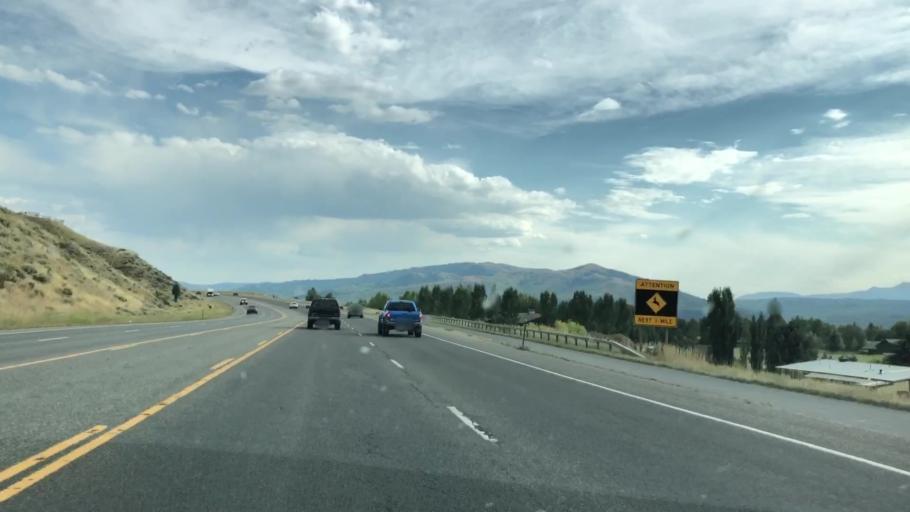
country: US
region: Wyoming
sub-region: Teton County
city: Rafter J Ranch
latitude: 43.4386
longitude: -110.7870
